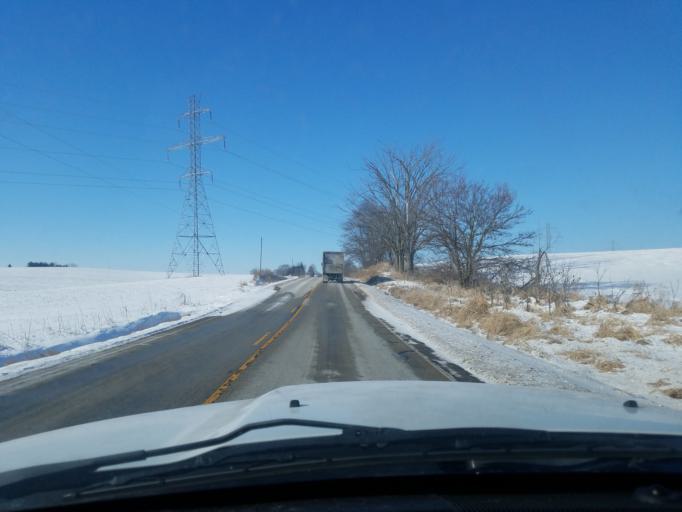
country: US
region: Indiana
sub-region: Noble County
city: Avilla
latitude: 41.3946
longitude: -85.2751
